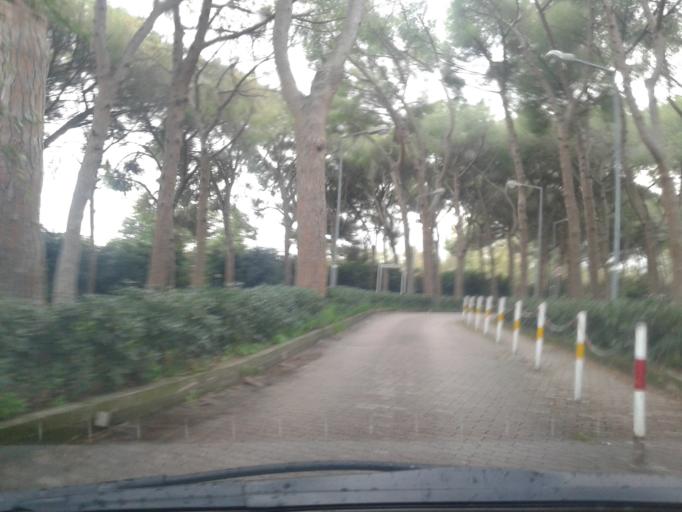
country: IT
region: Sicily
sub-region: Palermo
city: Monreale
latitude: 38.0943
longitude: 13.3105
